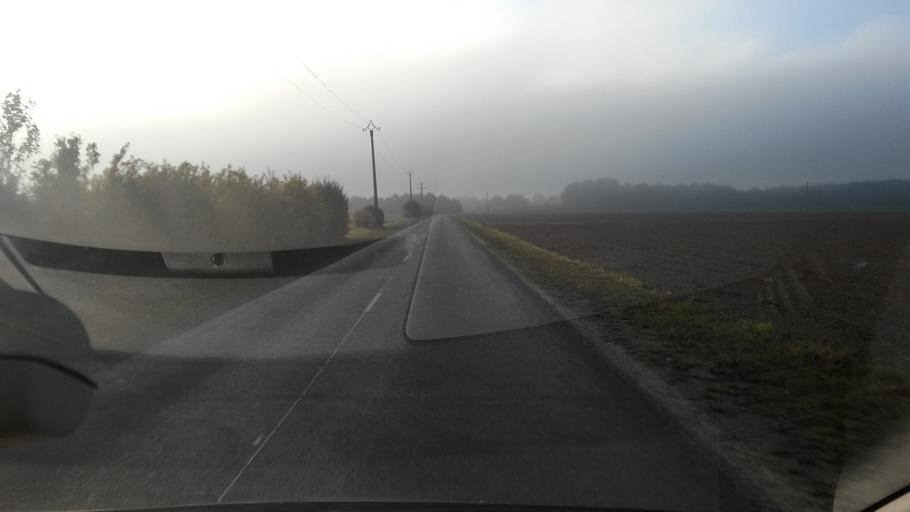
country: FR
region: Champagne-Ardenne
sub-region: Departement de la Marne
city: Connantre
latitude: 48.7352
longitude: 3.9022
